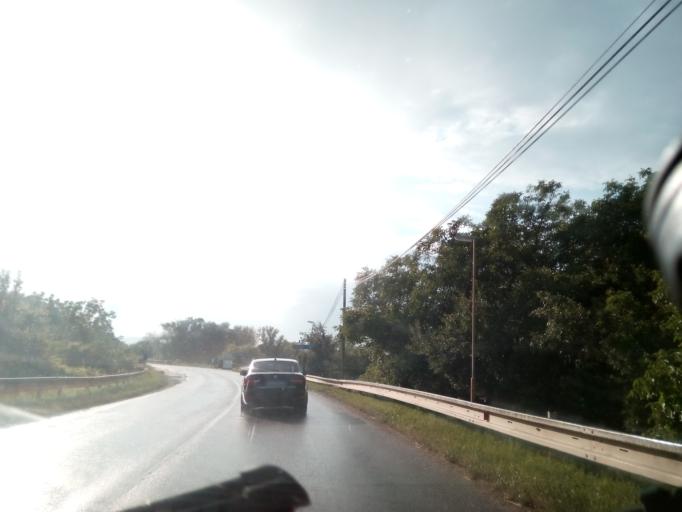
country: SK
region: Kosicky
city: Kosice
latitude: 48.6566
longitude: 21.3584
